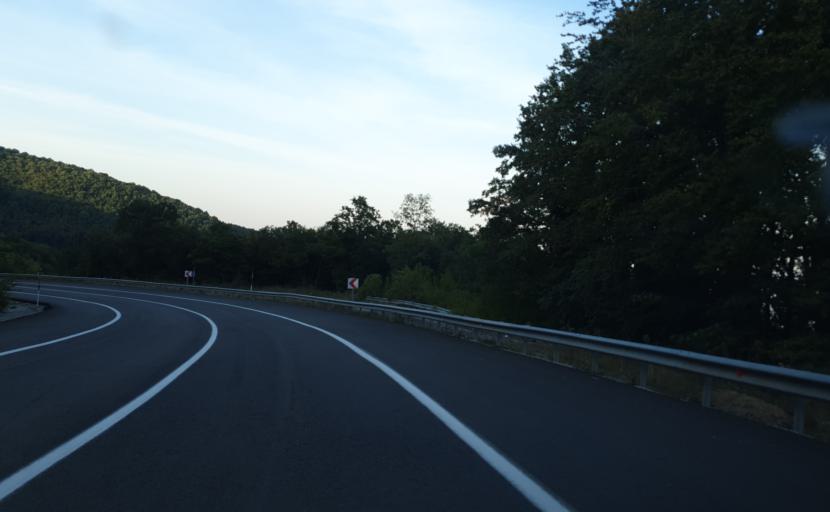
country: TR
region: Kirklareli
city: Sergen
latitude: 41.8044
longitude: 27.7387
